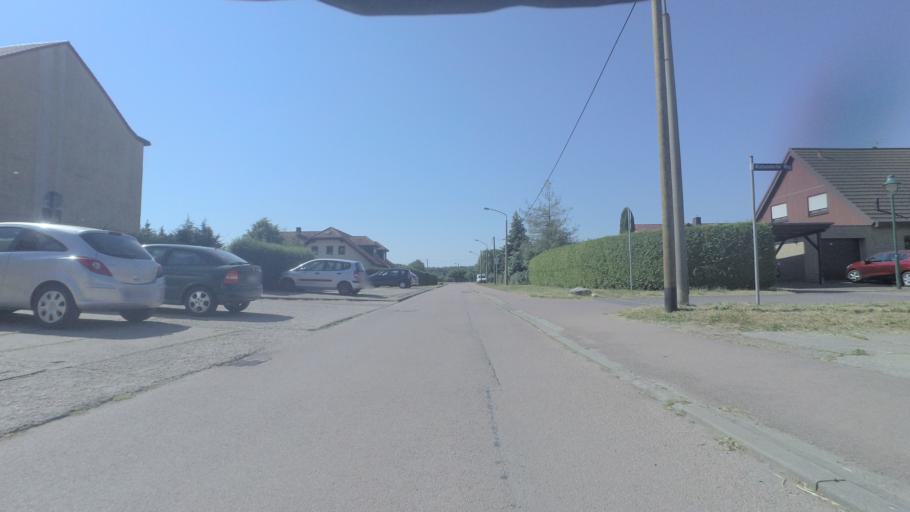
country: DE
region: Saxony-Anhalt
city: Vockerode
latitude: 51.8435
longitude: 12.3468
